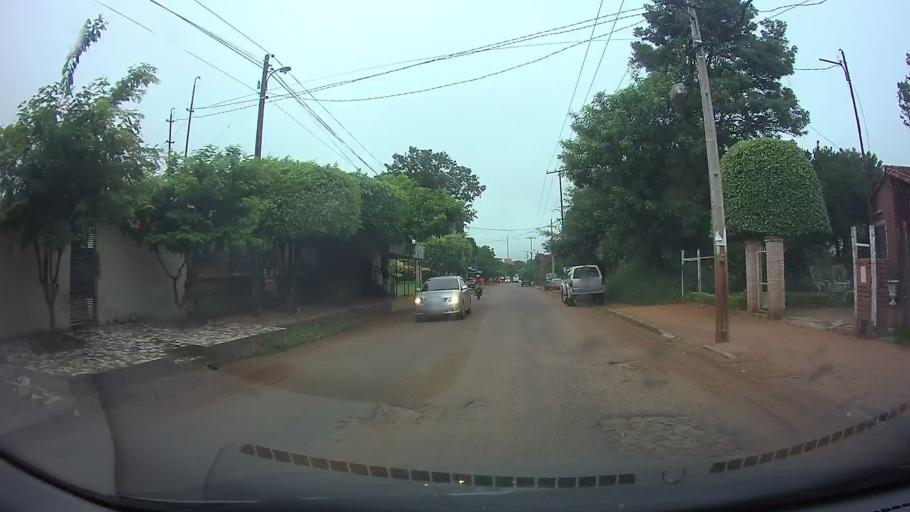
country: PY
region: Central
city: Itaugua
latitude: -25.3882
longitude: -57.3515
